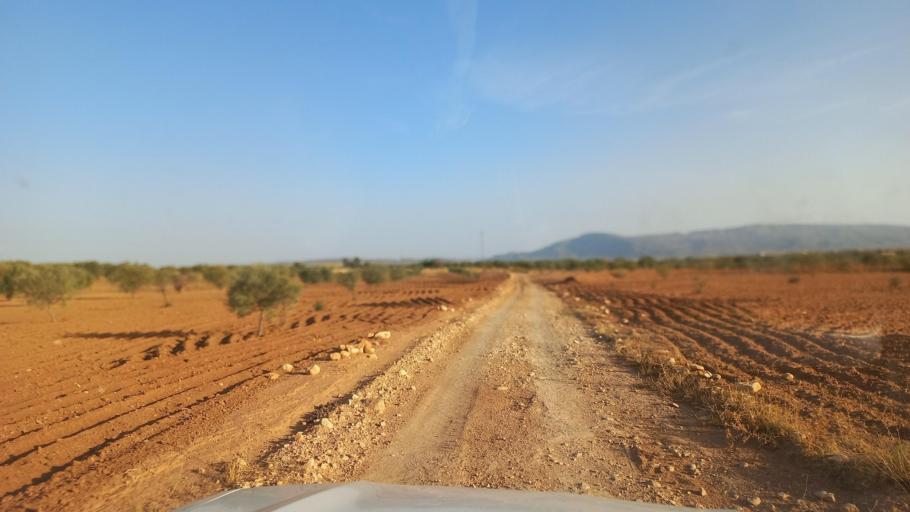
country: TN
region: Al Qasrayn
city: Kasserine
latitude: 35.2590
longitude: 8.9062
